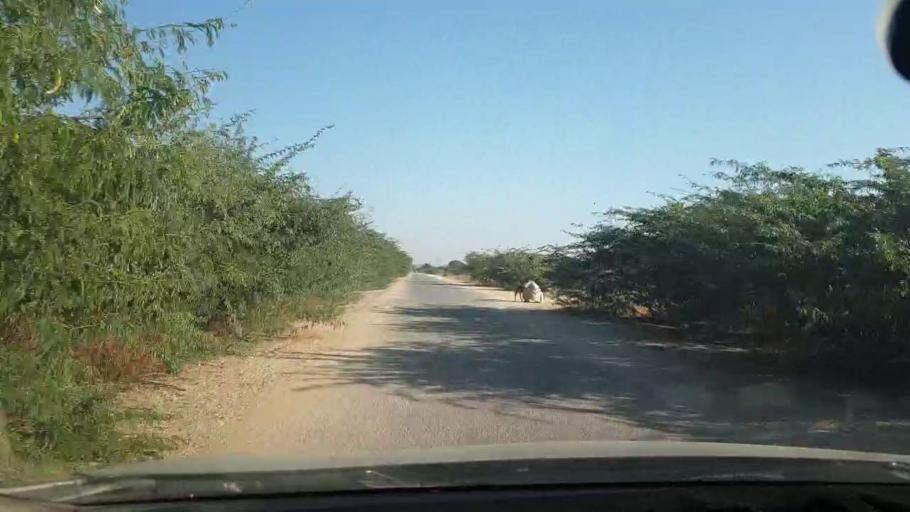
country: PK
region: Sindh
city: Malir Cantonment
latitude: 25.1706
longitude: 67.2009
